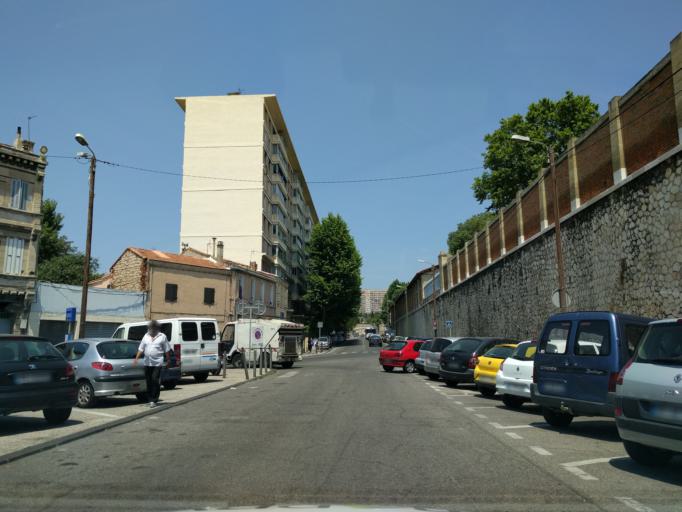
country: FR
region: Provence-Alpes-Cote d'Azur
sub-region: Departement des Bouches-du-Rhone
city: Marseille 14
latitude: 43.3372
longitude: 5.3580
